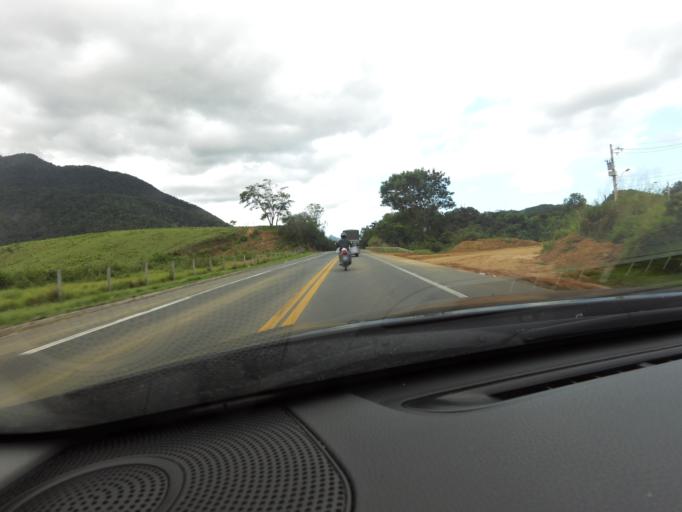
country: BR
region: Espirito Santo
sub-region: Guarapari
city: Guarapari
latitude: -20.6260
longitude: -40.5261
